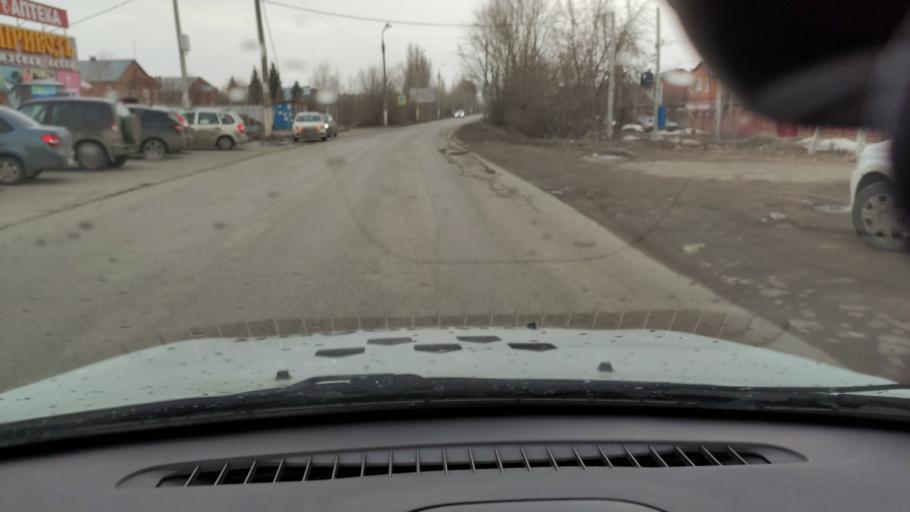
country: RU
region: Samara
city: Tol'yatti
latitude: 53.5589
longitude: 49.3946
